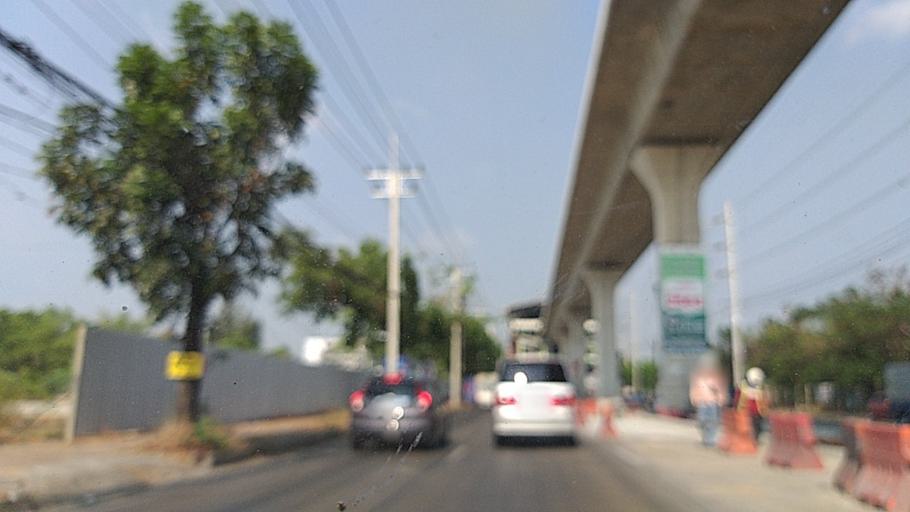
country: TH
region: Bangkok
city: Sai Mai
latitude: 13.9322
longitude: 100.6488
